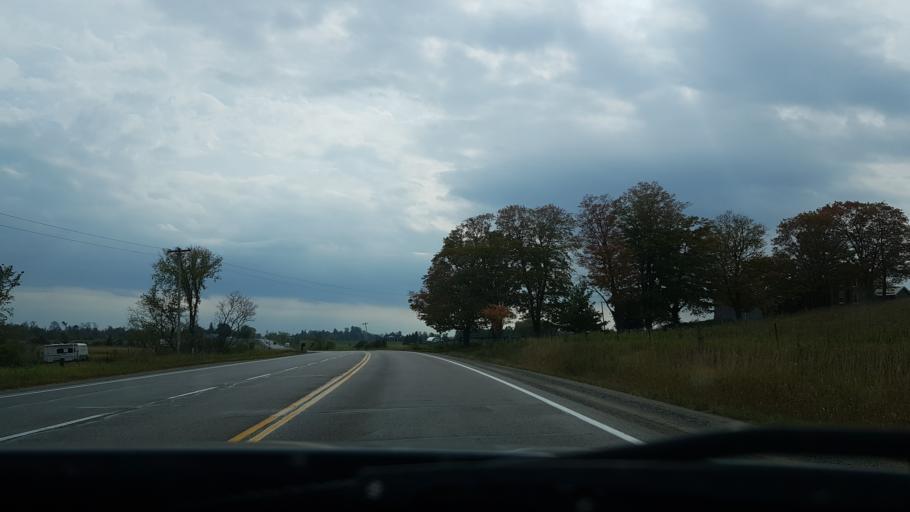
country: CA
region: Ontario
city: Omemee
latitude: 44.4569
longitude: -78.7672
